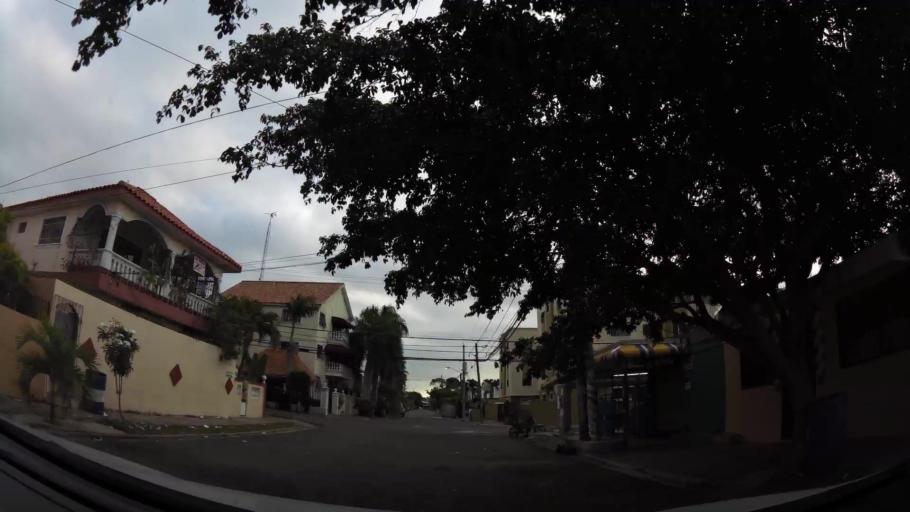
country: DO
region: Nacional
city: Bella Vista
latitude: 18.4319
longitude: -69.9619
